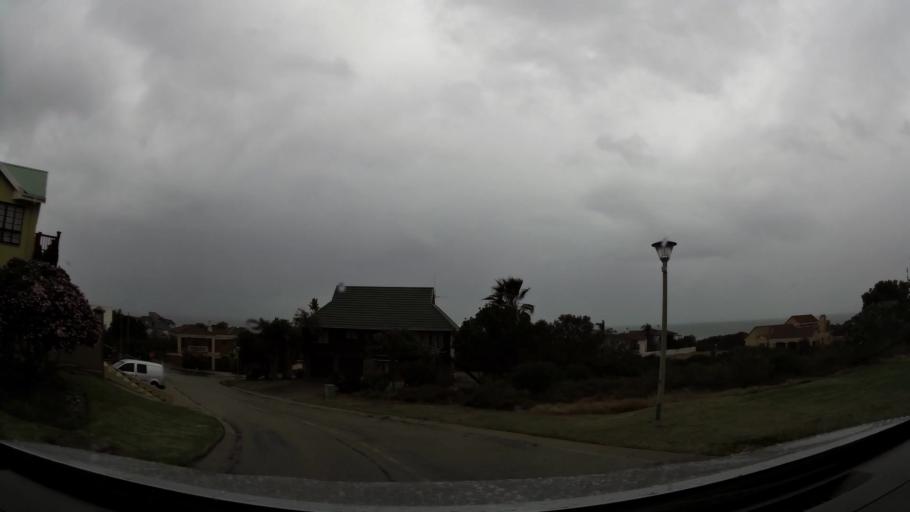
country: ZA
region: Western Cape
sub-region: Eden District Municipality
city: Mossel Bay
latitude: -34.0469
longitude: 22.2836
